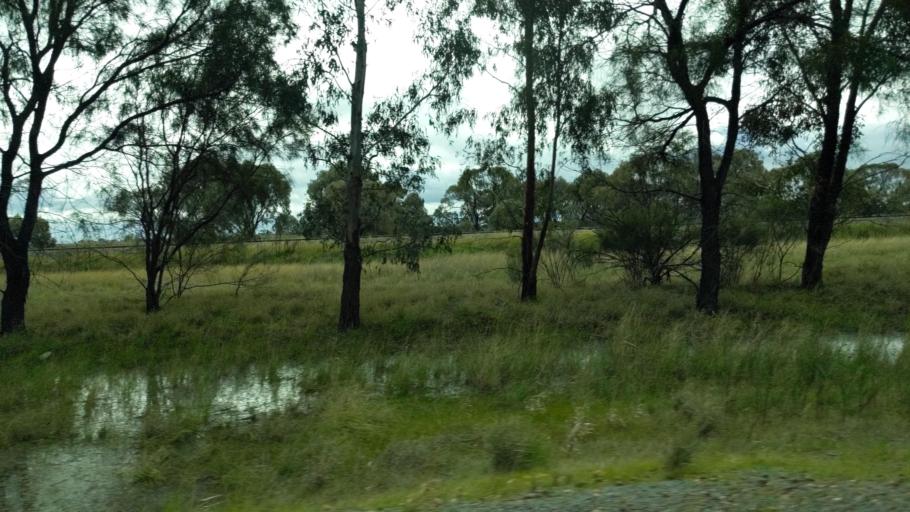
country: AU
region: New South Wales
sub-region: Coolamon
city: Coolamon
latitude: -34.7650
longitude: 146.9067
